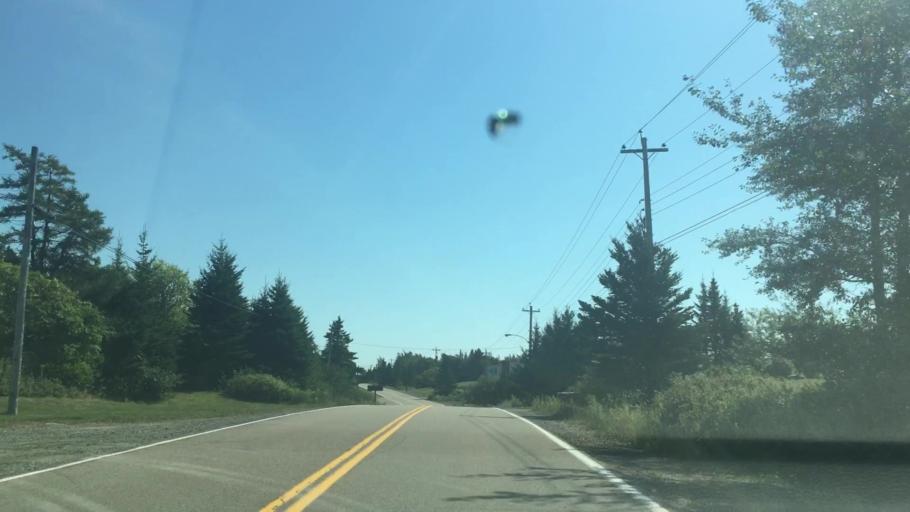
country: CA
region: Nova Scotia
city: Antigonish
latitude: 45.0255
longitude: -62.0263
